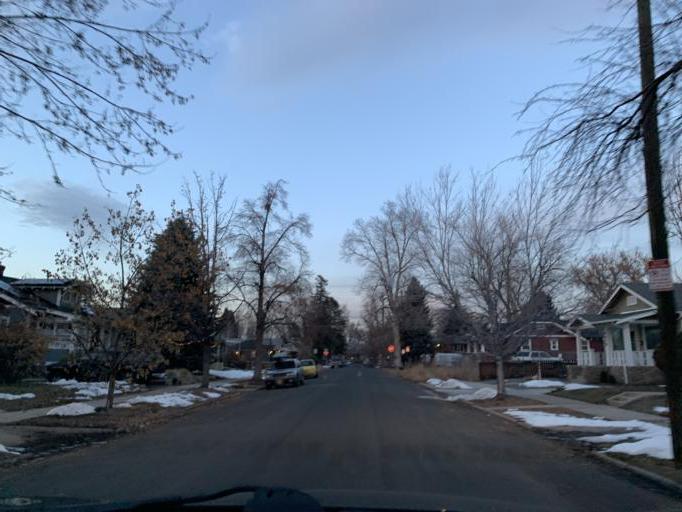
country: US
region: Colorado
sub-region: Adams County
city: Berkley
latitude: 39.7776
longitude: -105.0369
